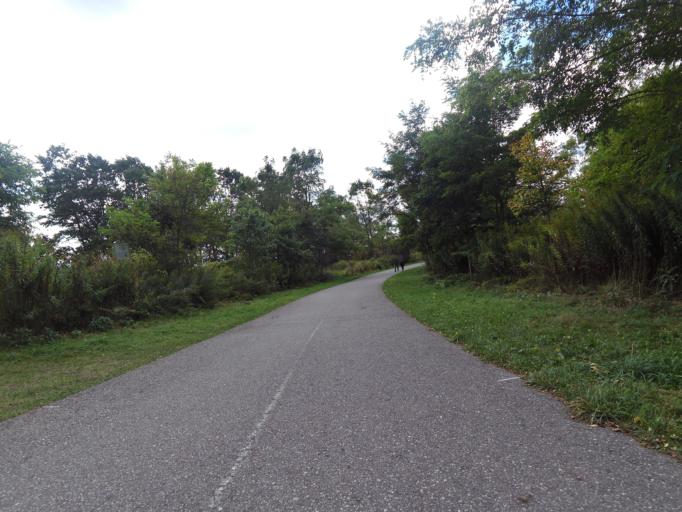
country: CA
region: Ontario
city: Ajax
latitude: 43.7959
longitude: -79.1167
